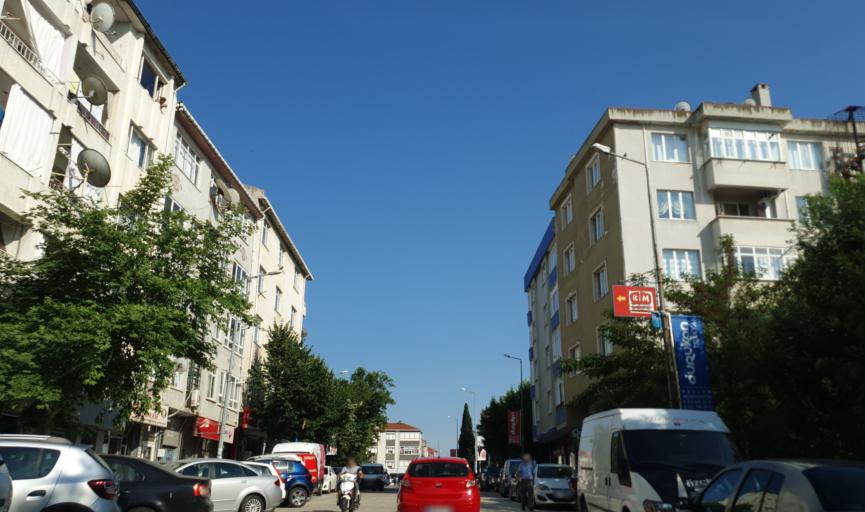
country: TR
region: Tekirdag
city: Saray
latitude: 41.4432
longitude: 27.9193
